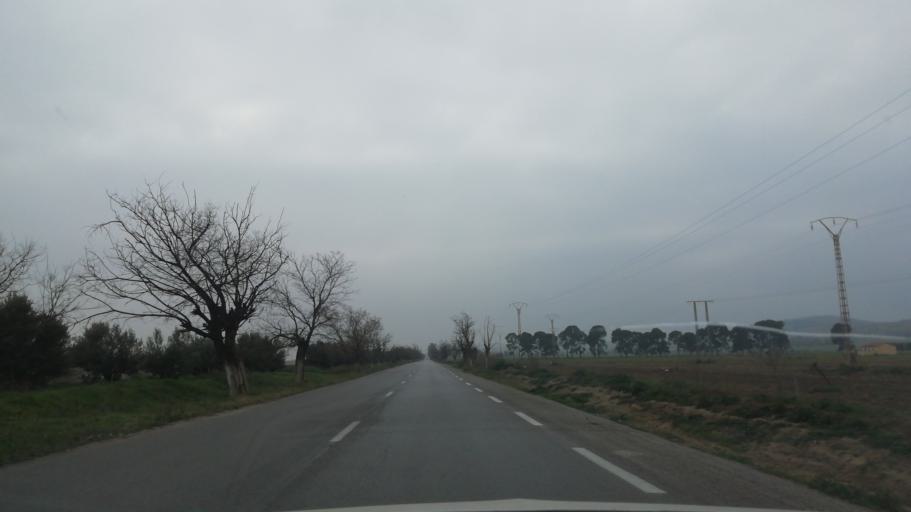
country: DZ
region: Sidi Bel Abbes
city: Sfizef
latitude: 35.2237
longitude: -0.2820
